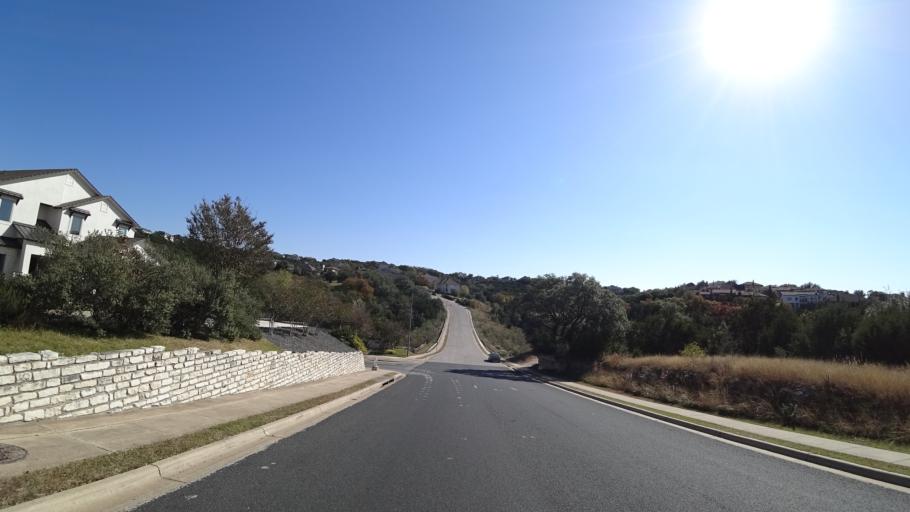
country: US
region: Texas
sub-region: Travis County
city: Lost Creek
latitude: 30.3661
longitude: -97.8599
